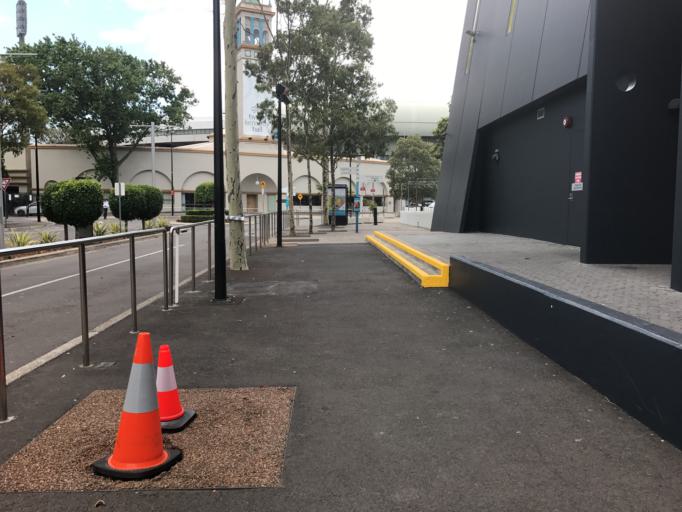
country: AU
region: New South Wales
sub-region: Woollahra
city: Paddington
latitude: -33.8940
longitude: 151.2250
